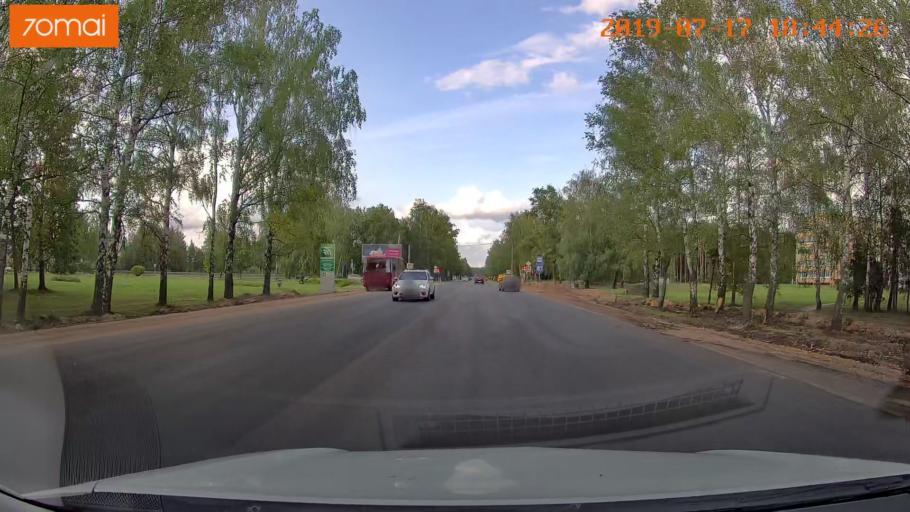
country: BY
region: Mogilev
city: Asipovichy
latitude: 53.3204
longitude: 28.6484
